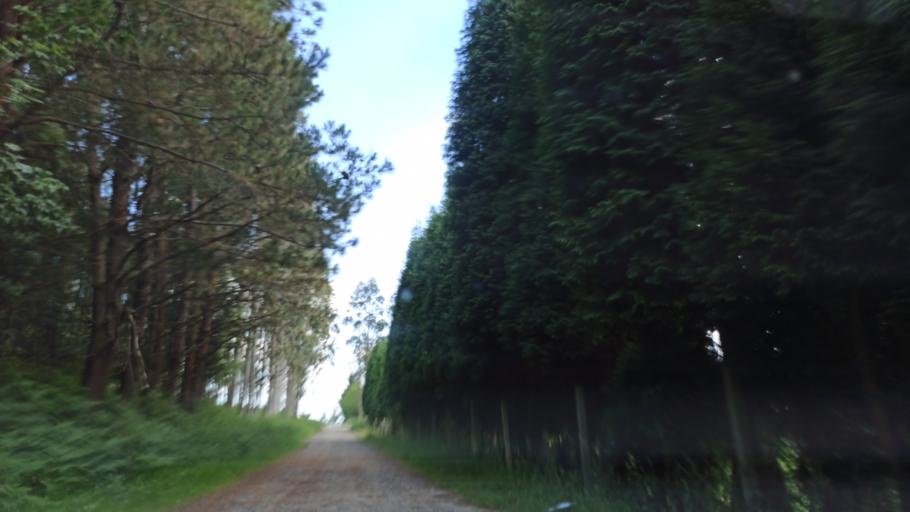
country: ES
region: Galicia
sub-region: Provincia da Coruna
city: Santa Comba
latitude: 43.0767
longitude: -8.7173
